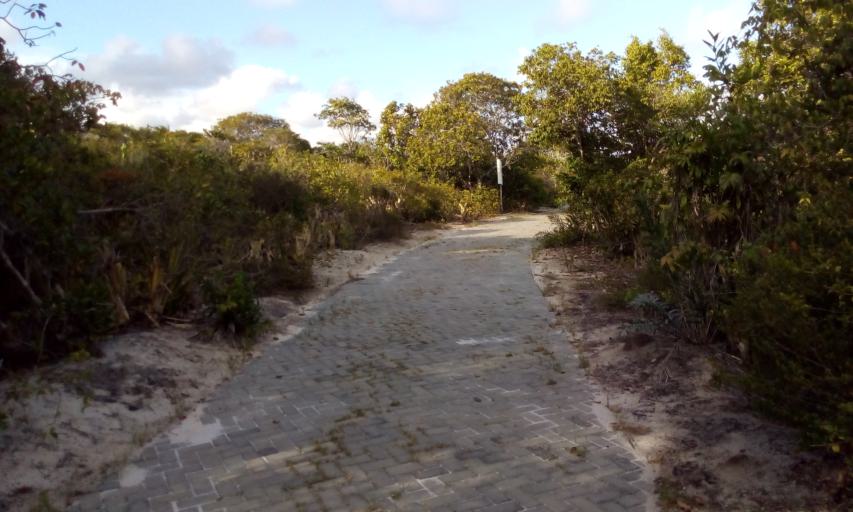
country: BR
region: Bahia
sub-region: Mata De Sao Joao
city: Mata de Sao Joao
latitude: -12.5662
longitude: -38.0047
